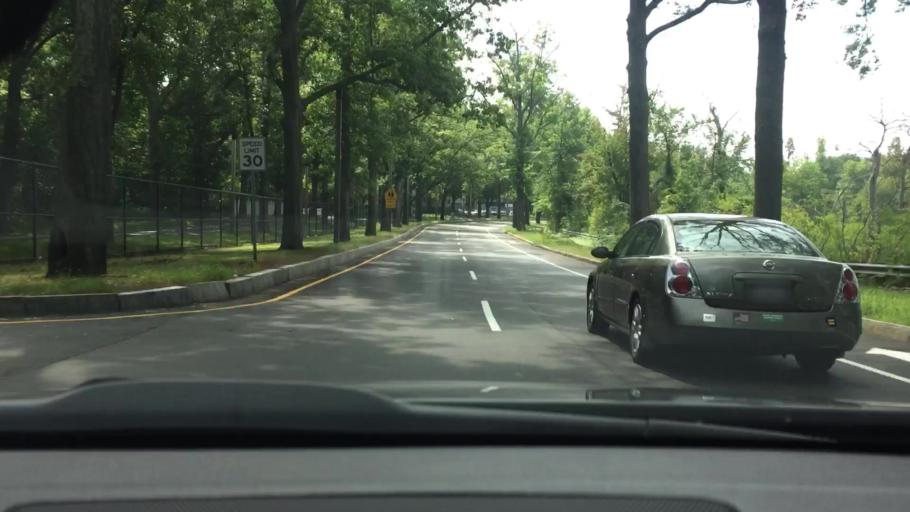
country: US
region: Massachusetts
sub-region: Norfolk County
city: Dedham
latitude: 42.2828
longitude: -71.1717
